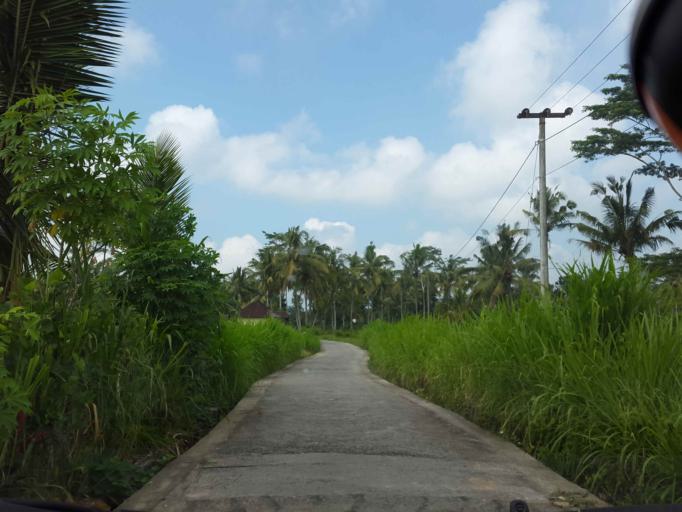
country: ID
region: Bali
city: Banjar Bebalang
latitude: -8.4671
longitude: 115.3826
